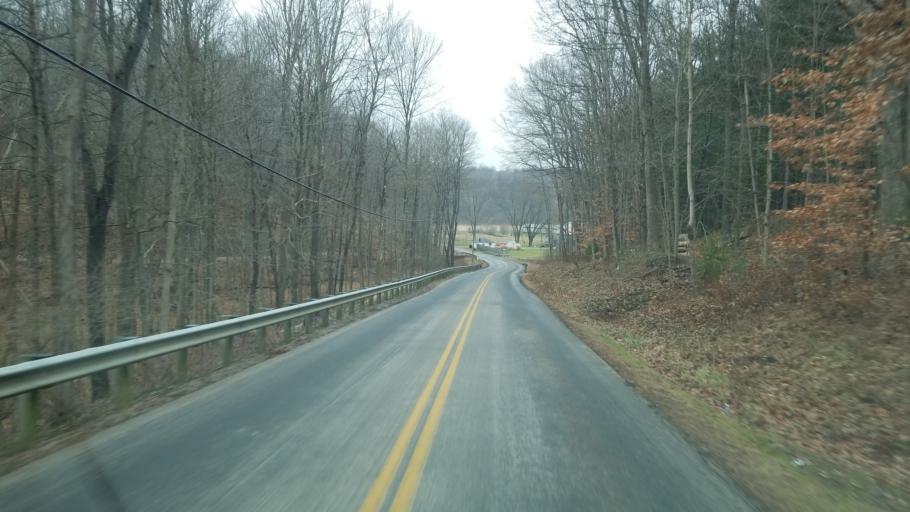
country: US
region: Ohio
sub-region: Holmes County
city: Millersburg
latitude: 40.5237
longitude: -81.9006
